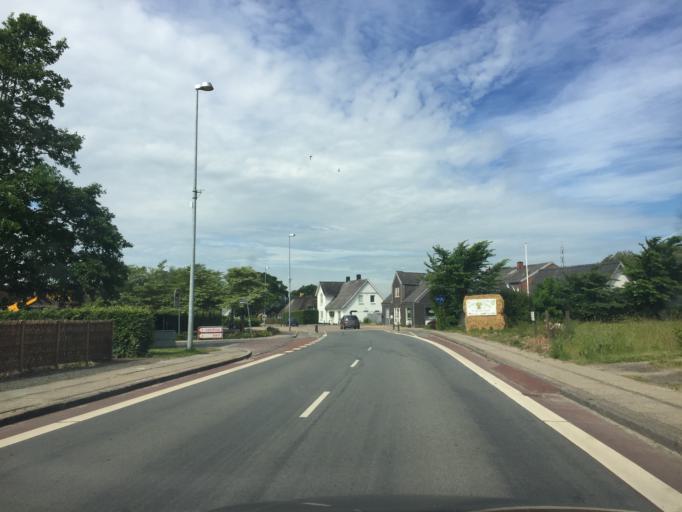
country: DK
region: South Denmark
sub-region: Faaborg-Midtfyn Kommune
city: Ringe
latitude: 55.2194
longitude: 10.6011
